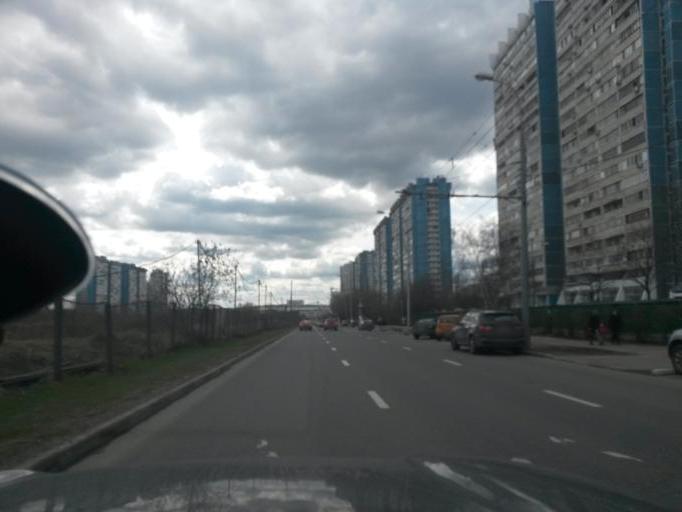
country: RU
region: Moscow
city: Yasenevo
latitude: 55.6052
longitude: 37.5317
